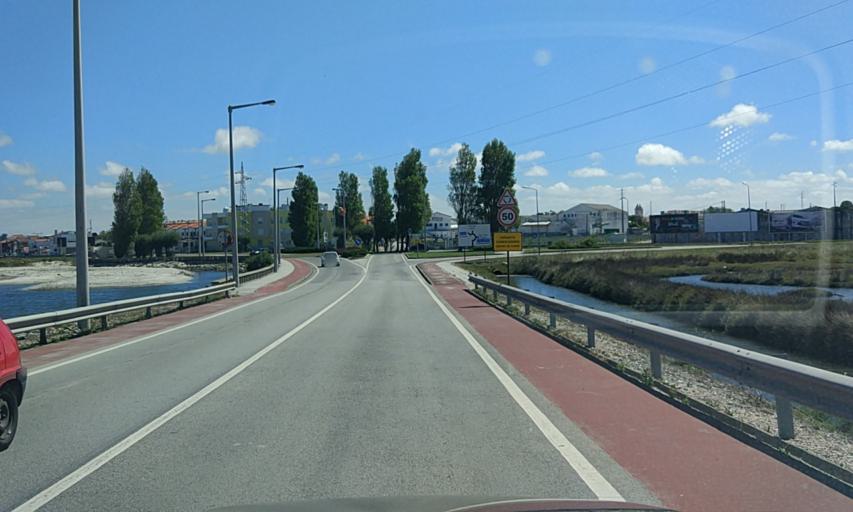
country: PT
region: Aveiro
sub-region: Ilhavo
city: Ilhavo
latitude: 40.6072
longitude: -8.6811
